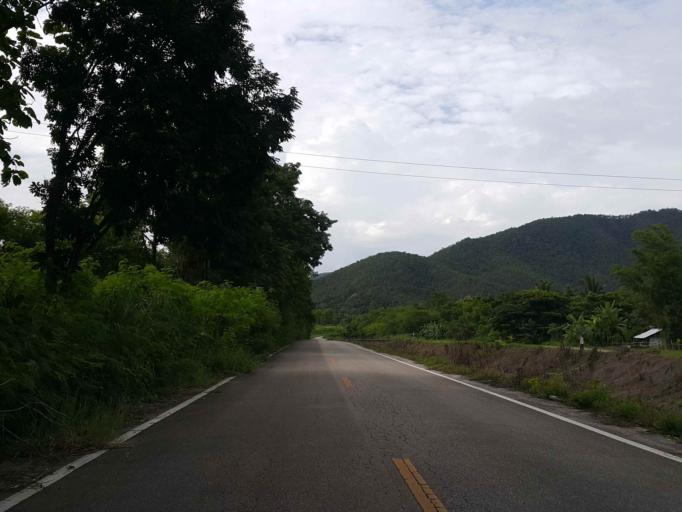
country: TH
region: Chiang Mai
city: San Sai
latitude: 18.9295
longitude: 99.1428
